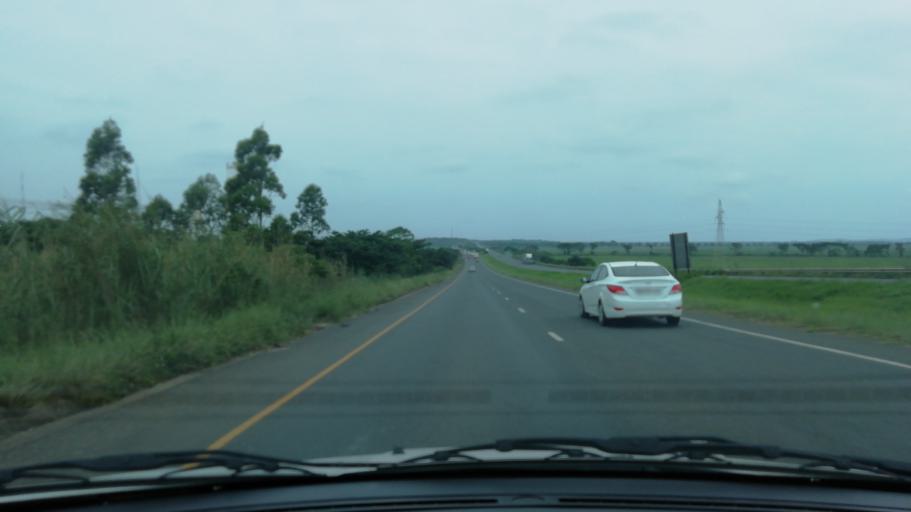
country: ZA
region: KwaZulu-Natal
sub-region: uThungulu District Municipality
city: Empangeni
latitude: -28.7710
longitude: 31.9401
